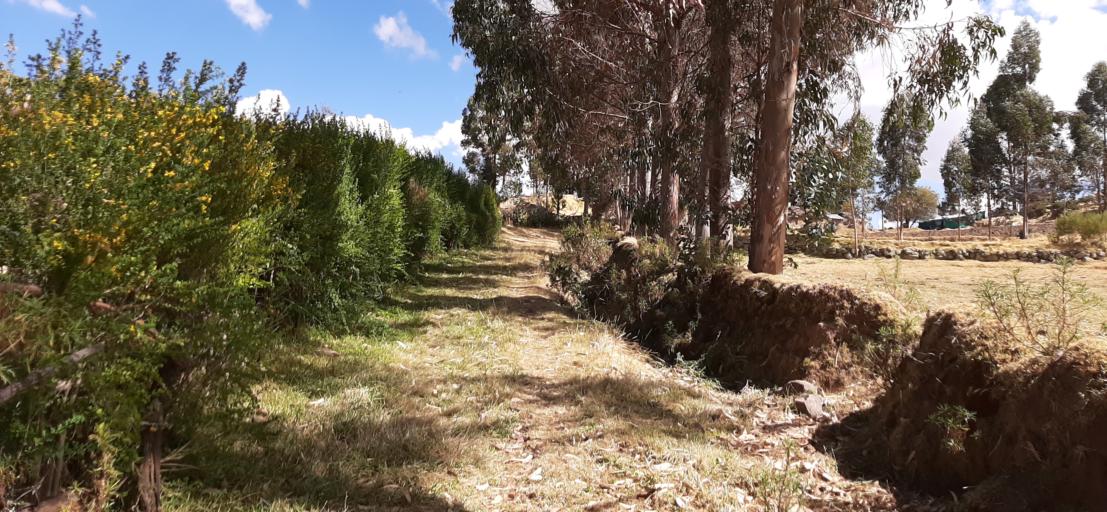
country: PE
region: Cusco
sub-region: Provincia de Chumbivilcas
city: Chamaca
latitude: -14.2579
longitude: -71.8790
